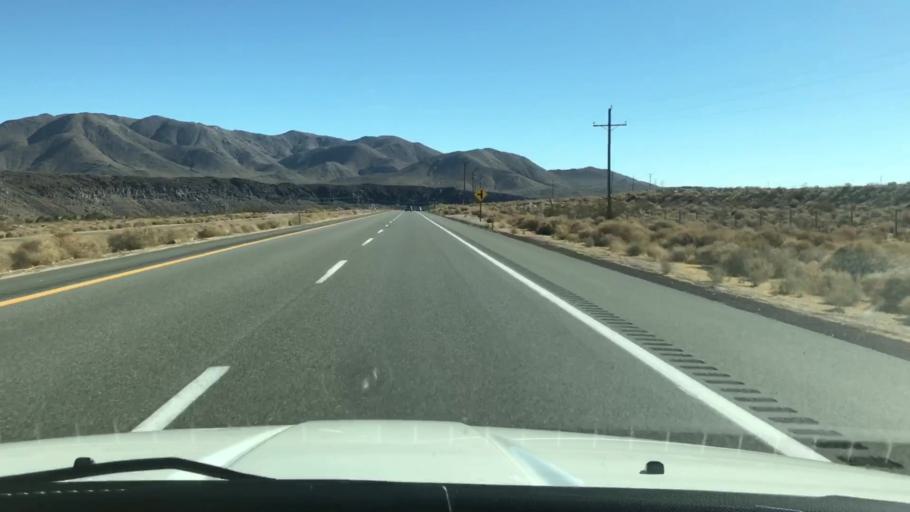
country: US
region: California
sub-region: Kern County
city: Inyokern
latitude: 35.9605
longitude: -117.9143
